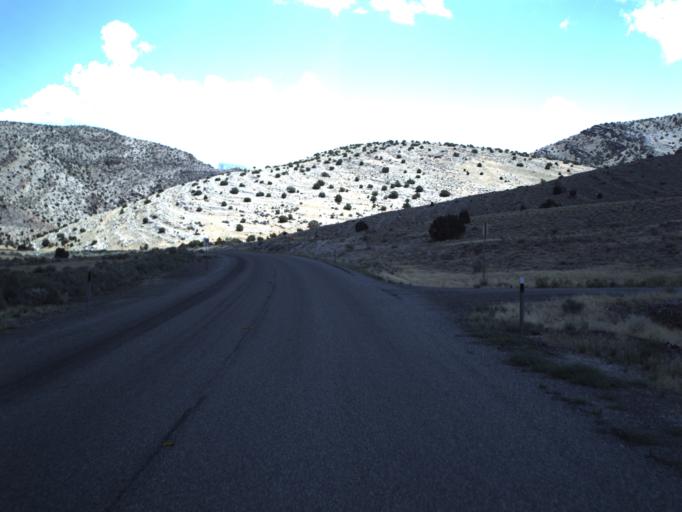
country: US
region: Utah
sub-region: Beaver County
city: Milford
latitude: 39.0789
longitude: -113.6095
